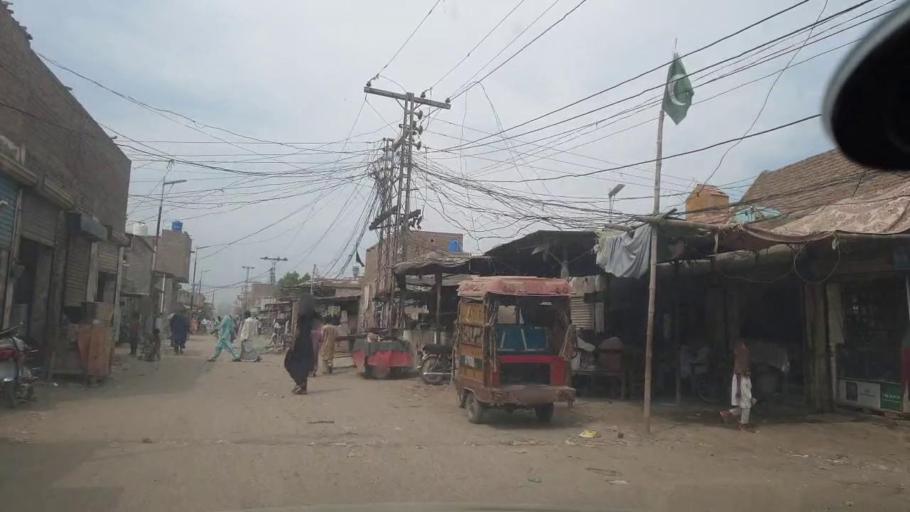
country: PK
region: Sindh
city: Jacobabad
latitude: 28.2724
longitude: 68.4380
